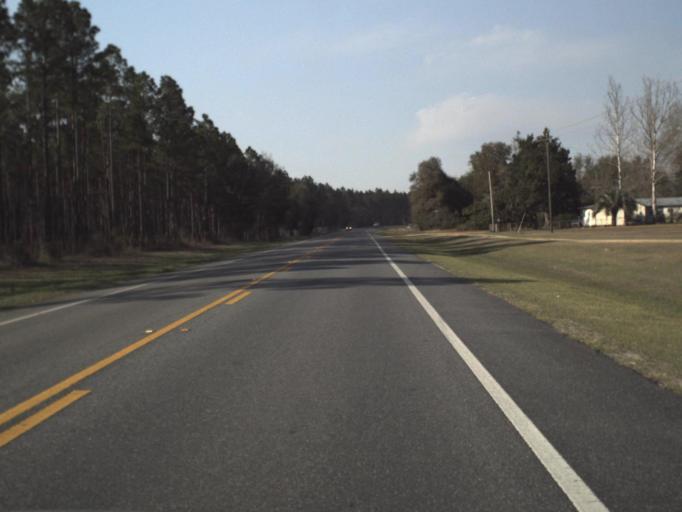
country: US
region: Florida
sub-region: Calhoun County
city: Blountstown
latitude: 30.5067
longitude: -85.2002
